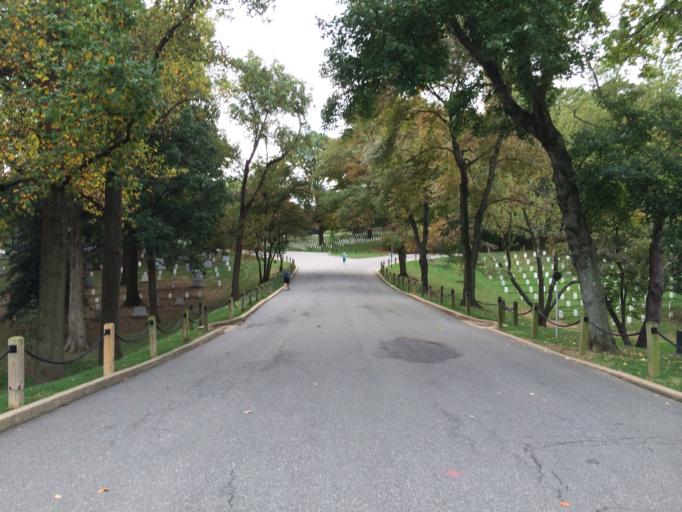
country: US
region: Virginia
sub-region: Arlington County
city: Arlington
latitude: 38.8787
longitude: -77.0710
